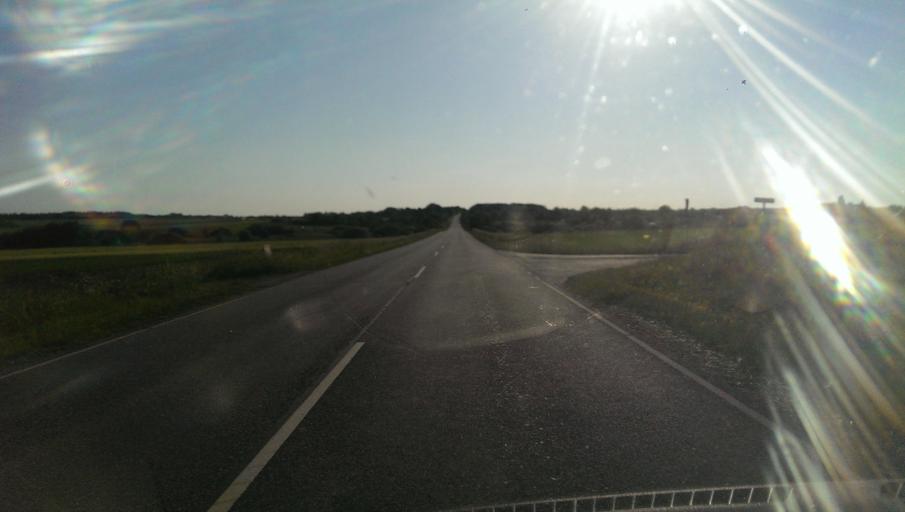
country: DK
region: South Denmark
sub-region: Esbjerg Kommune
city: Tjaereborg
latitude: 55.5264
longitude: 8.6253
